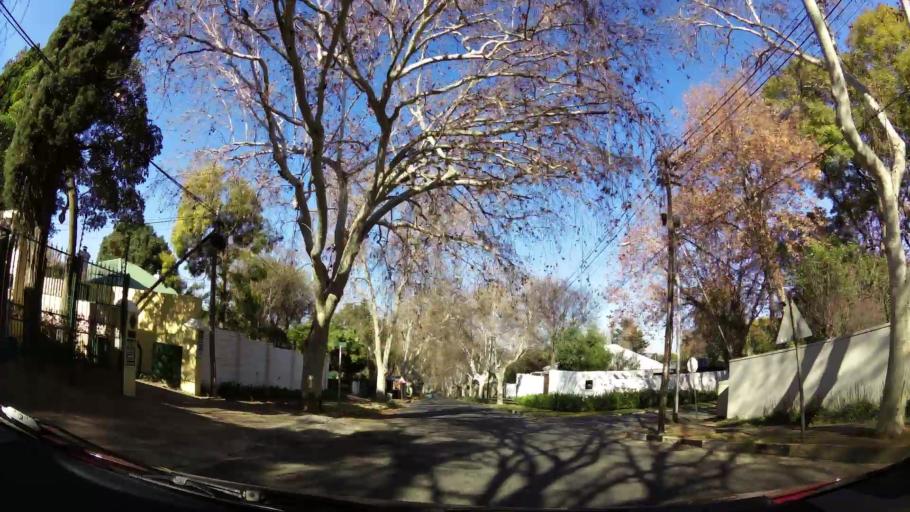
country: ZA
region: Gauteng
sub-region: City of Johannesburg Metropolitan Municipality
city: Johannesburg
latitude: -26.1464
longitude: 28.0318
